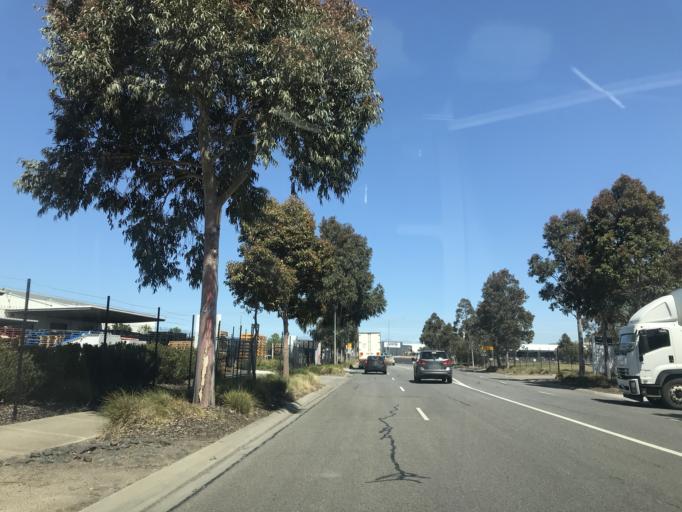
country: AU
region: Victoria
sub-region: Hobsons Bay
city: Laverton
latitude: -37.8401
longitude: 144.7719
